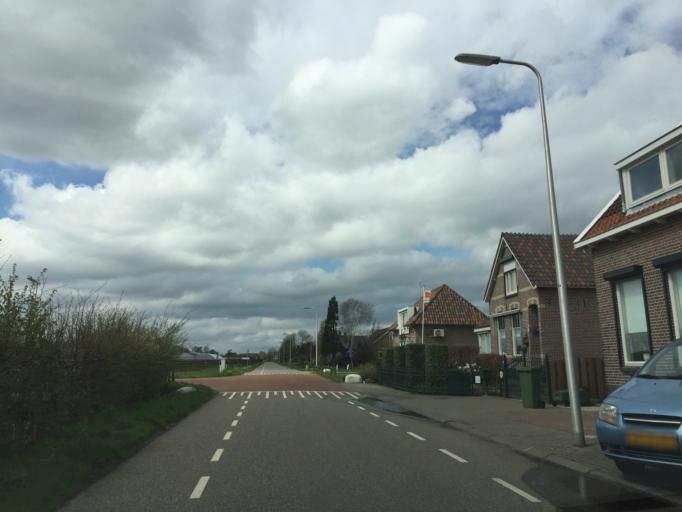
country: NL
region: South Holland
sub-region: Gemeente Waddinxveen
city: Vondelwijk
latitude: 52.0582
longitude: 4.6772
